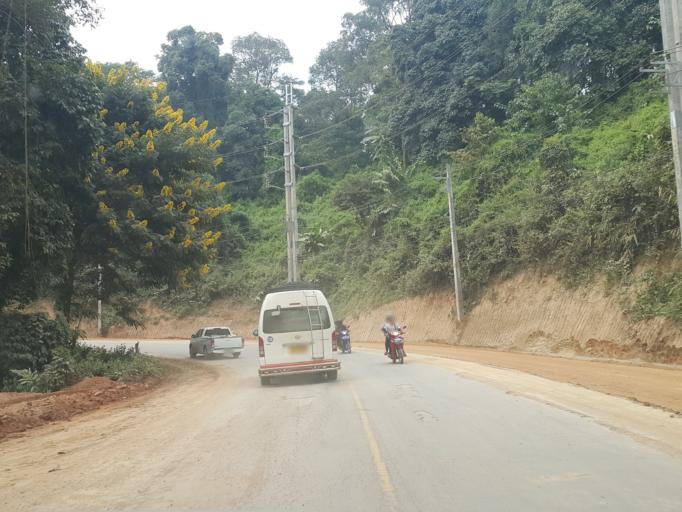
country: TH
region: Chiang Mai
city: Mae Taeng
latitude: 19.1277
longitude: 98.7069
